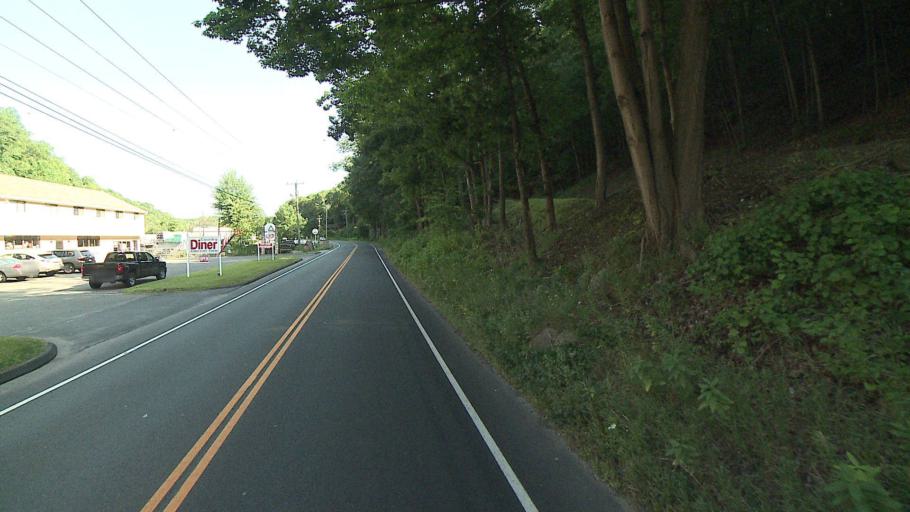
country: US
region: Connecticut
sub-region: Fairfield County
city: Georgetown
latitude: 41.2774
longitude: -73.4449
